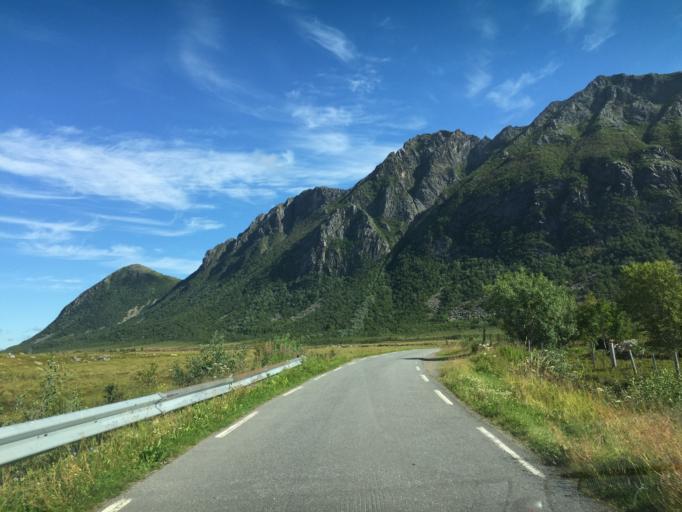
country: NO
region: Nordland
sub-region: Vagan
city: Svolvaer
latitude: 68.3984
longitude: 14.5672
